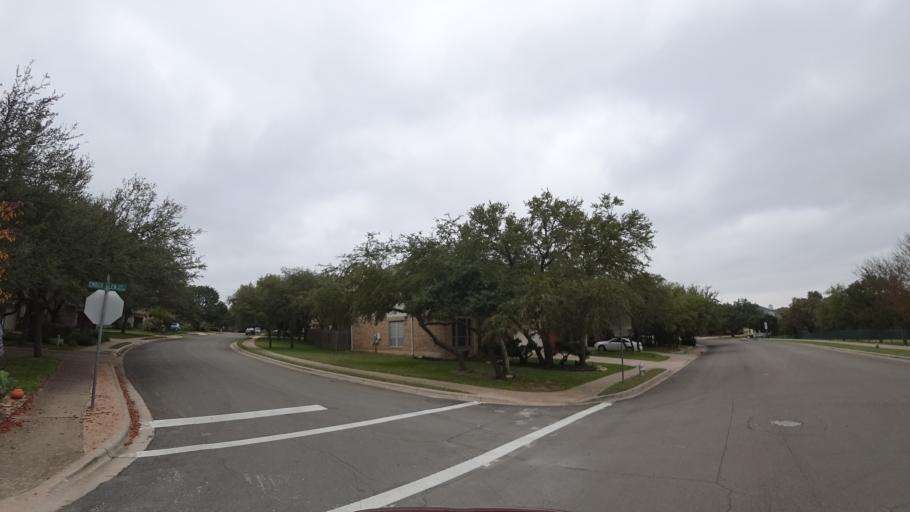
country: US
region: Texas
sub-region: Williamson County
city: Anderson Mill
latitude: 30.4370
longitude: -97.8256
